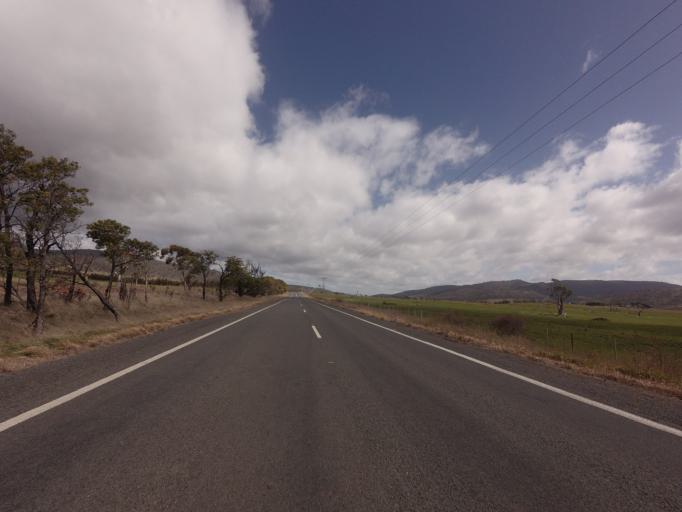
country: AU
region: Tasmania
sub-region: Northern Midlands
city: Evandale
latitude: -41.8105
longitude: 147.6483
